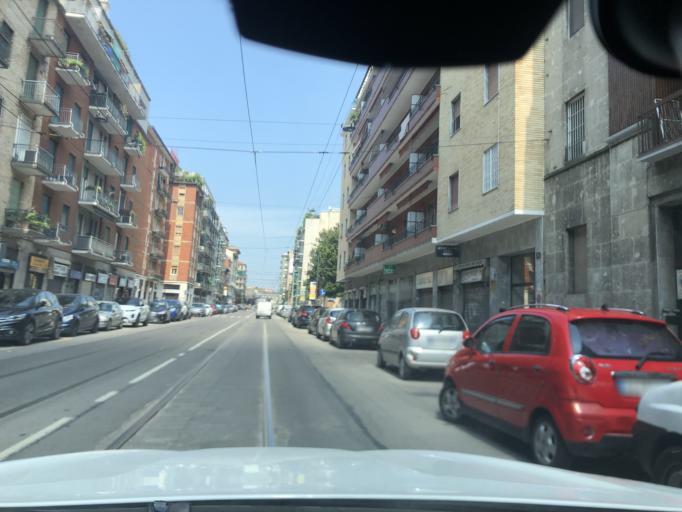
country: IT
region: Lombardy
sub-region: Citta metropolitana di Milano
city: Novate Milanese
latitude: 45.5005
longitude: 9.1676
